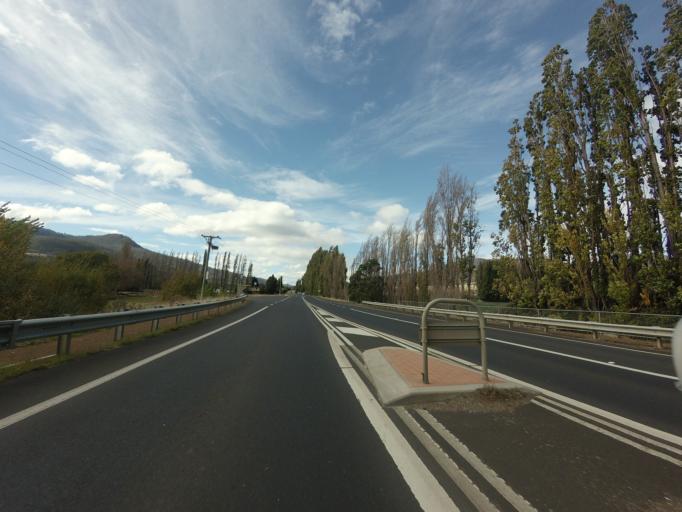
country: AU
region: Tasmania
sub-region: Derwent Valley
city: New Norfolk
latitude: -42.7817
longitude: 147.1087
